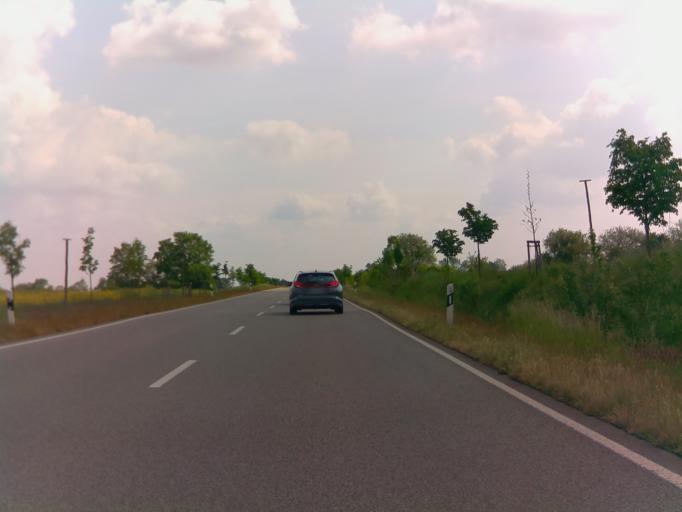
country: DE
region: Saxony-Anhalt
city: Uchtspringe
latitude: 52.5711
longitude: 11.6731
